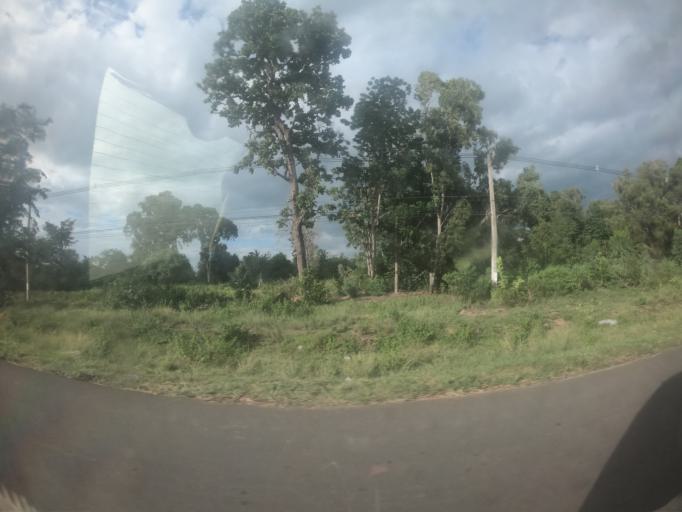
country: TH
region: Surin
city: Kap Choeng
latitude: 14.5251
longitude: 103.5371
